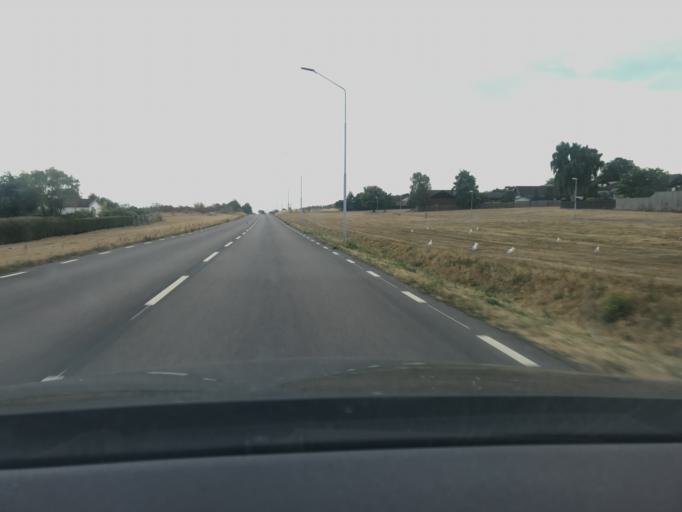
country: SE
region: Skane
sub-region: Simrishamns Kommun
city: Simrishamn
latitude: 55.5450
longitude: 14.3522
